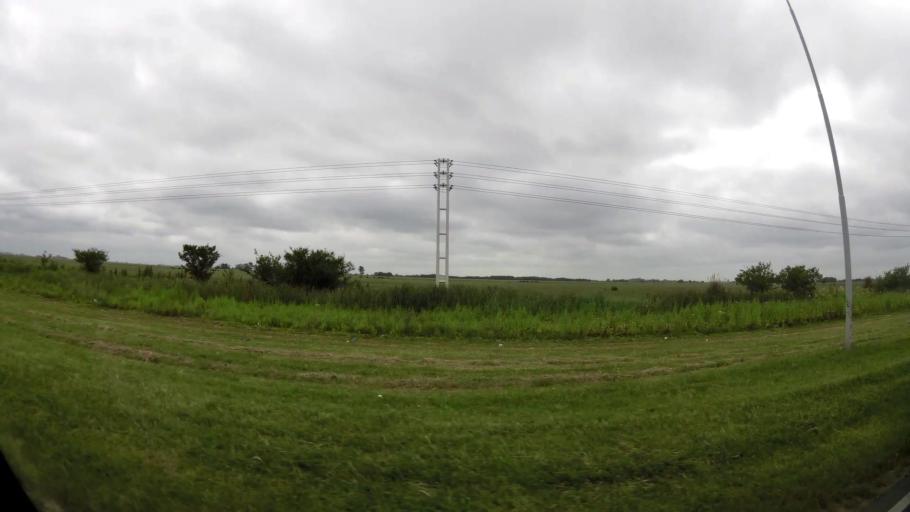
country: AR
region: Buenos Aires
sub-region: Partido de San Vicente
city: San Vicente
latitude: -34.9967
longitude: -58.4698
